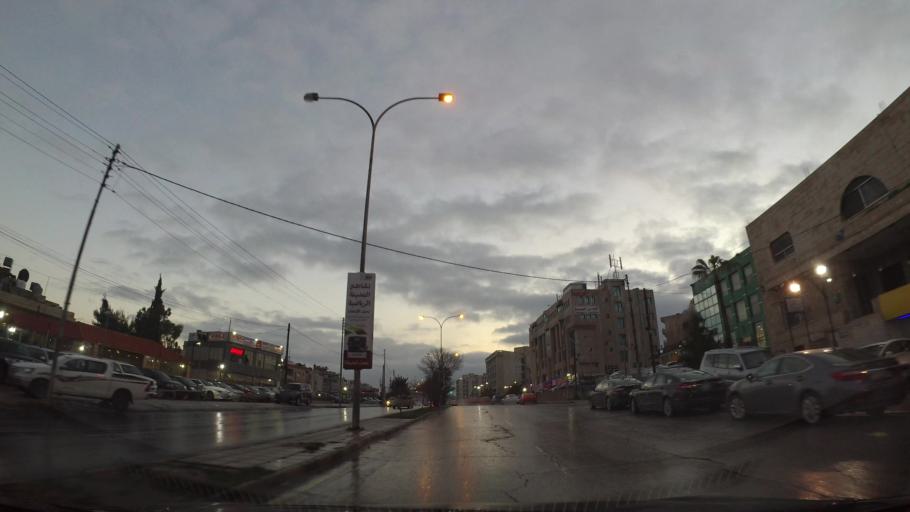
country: JO
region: Amman
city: Al Jubayhah
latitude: 31.9787
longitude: 35.8896
